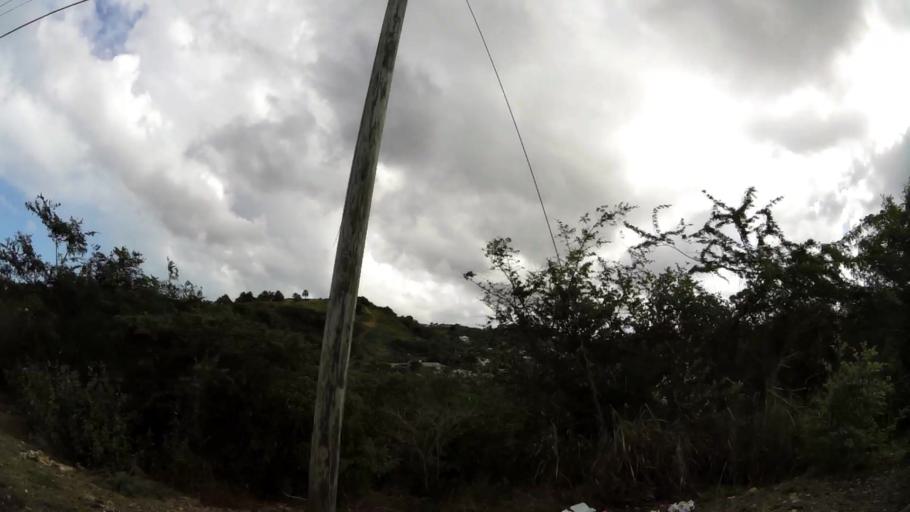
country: AG
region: Saint John
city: Saint John's
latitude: 17.1063
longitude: -61.8529
